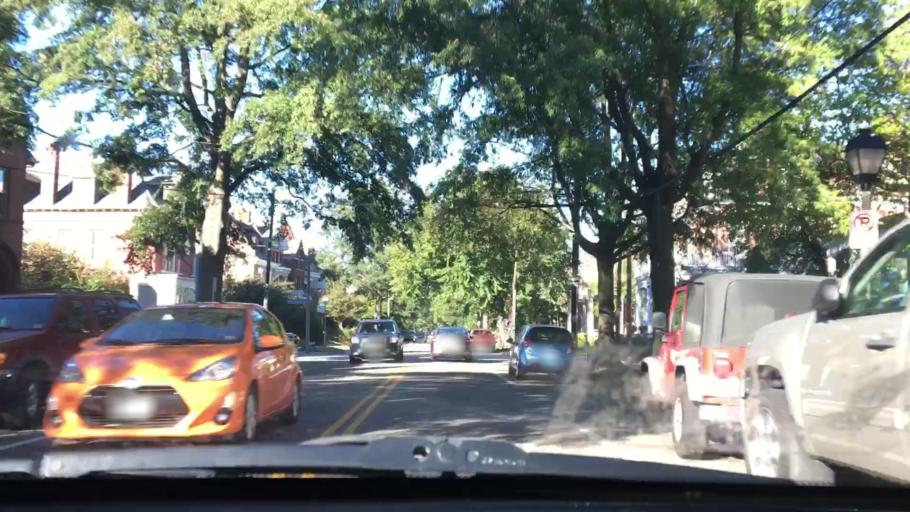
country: US
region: Virginia
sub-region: City of Norfolk
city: Norfolk
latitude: 36.8593
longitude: -76.2963
